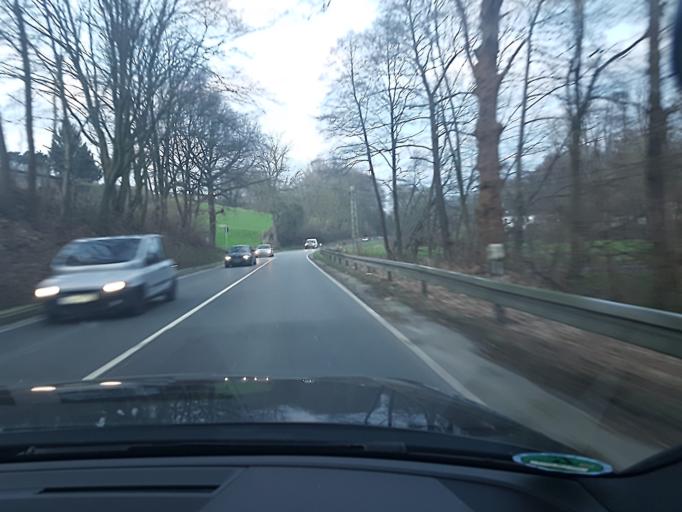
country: DE
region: North Rhine-Westphalia
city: Hattingen
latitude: 51.3790
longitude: 7.1954
